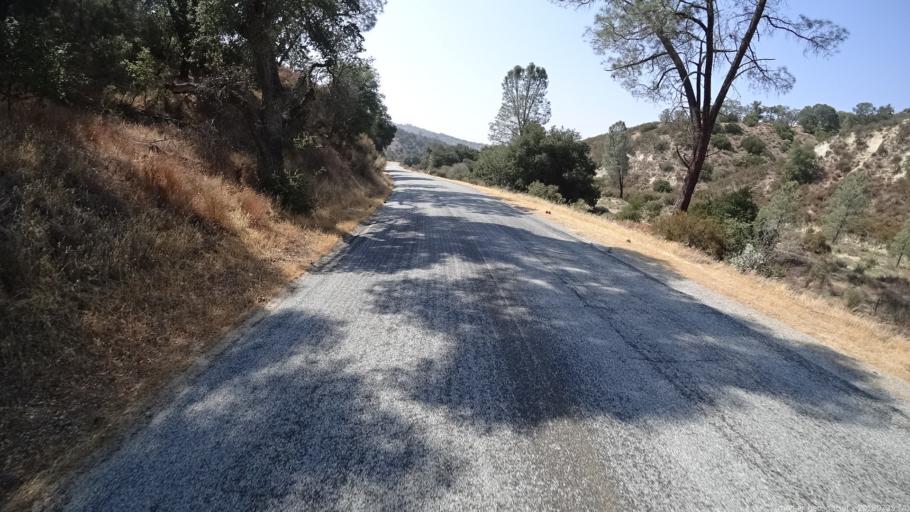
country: US
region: California
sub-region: San Luis Obispo County
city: San Miguel
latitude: 35.8904
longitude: -120.5595
